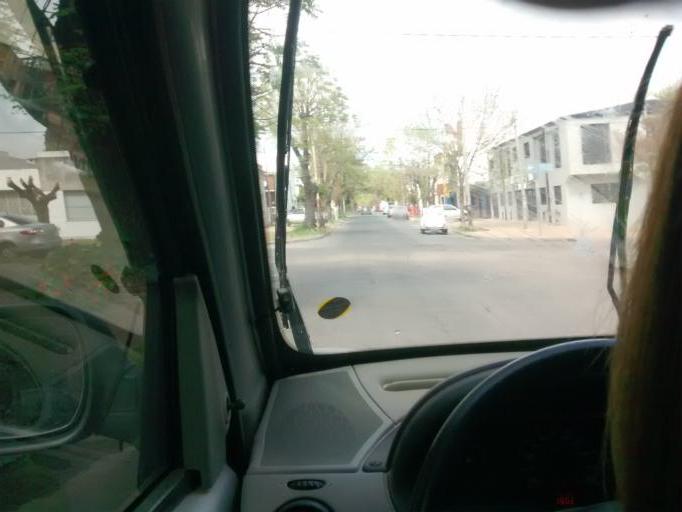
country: AR
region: Buenos Aires
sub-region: Partido de La Plata
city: La Plata
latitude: -34.9397
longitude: -57.9456
